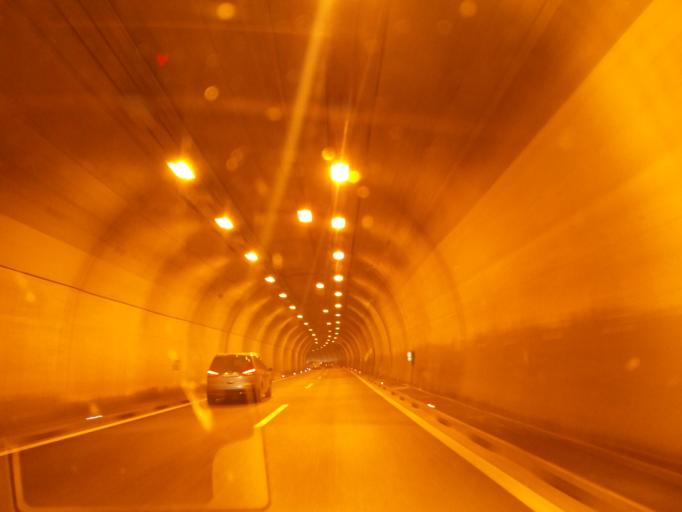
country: AT
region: Carinthia
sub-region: Politischer Bezirk Klagenfurt Land
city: Poggersdorf
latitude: 46.6424
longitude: 14.4288
